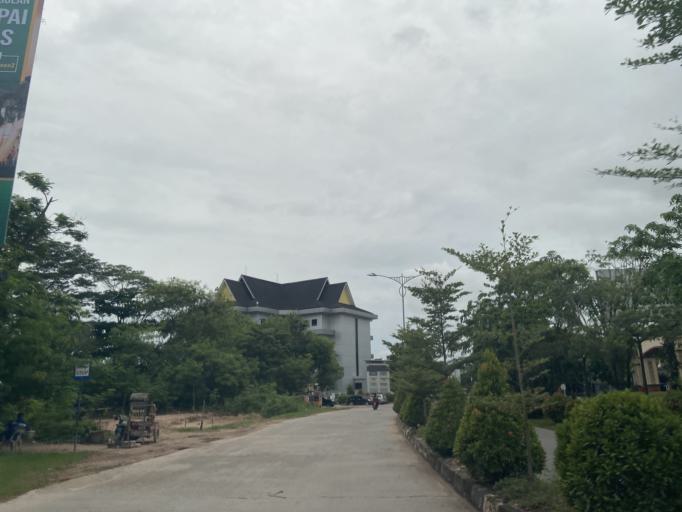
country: SG
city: Singapore
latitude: 1.1258
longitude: 104.0579
